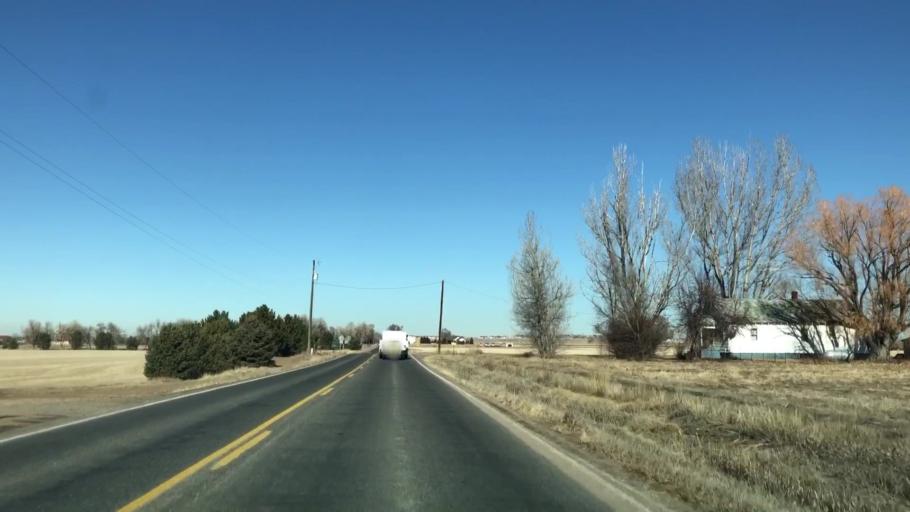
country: US
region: Colorado
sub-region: Weld County
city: Windsor
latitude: 40.4909
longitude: -104.9441
